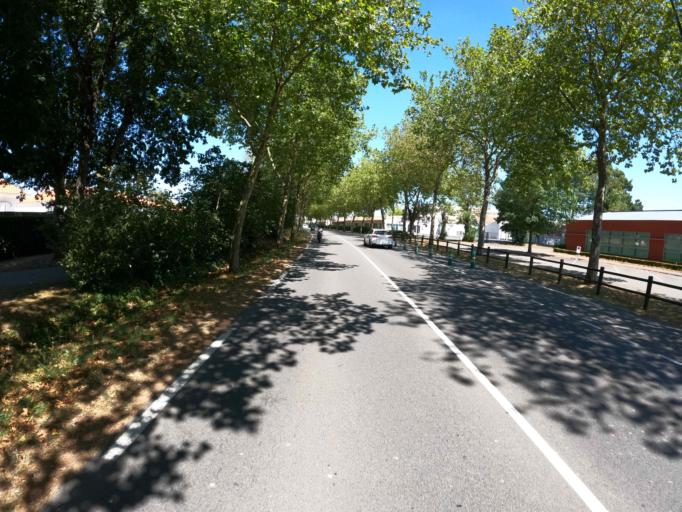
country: FR
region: Pays de la Loire
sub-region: Departement de la Vendee
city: Challans
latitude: 46.8378
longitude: -1.8664
